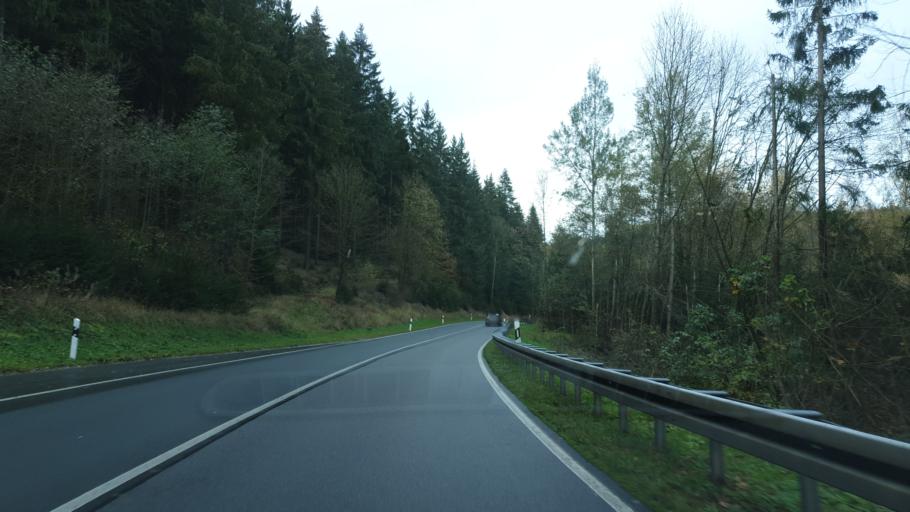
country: DE
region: Saxony
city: Eibenstock
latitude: 50.5021
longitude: 12.5620
